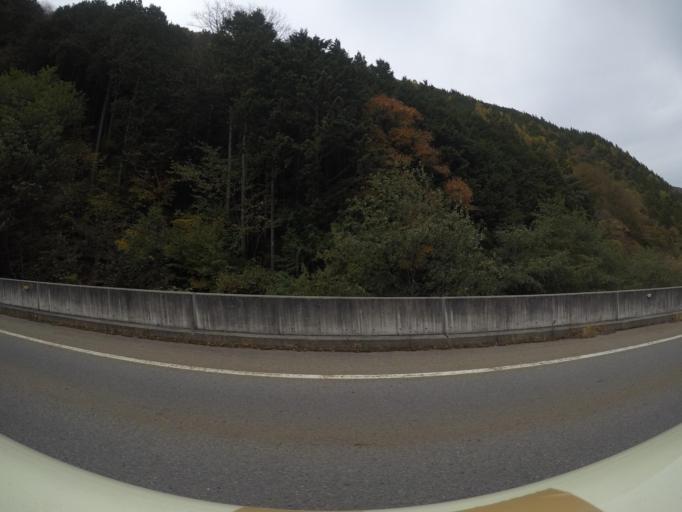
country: JP
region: Nagano
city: Ina
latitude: 35.8997
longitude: 137.8195
